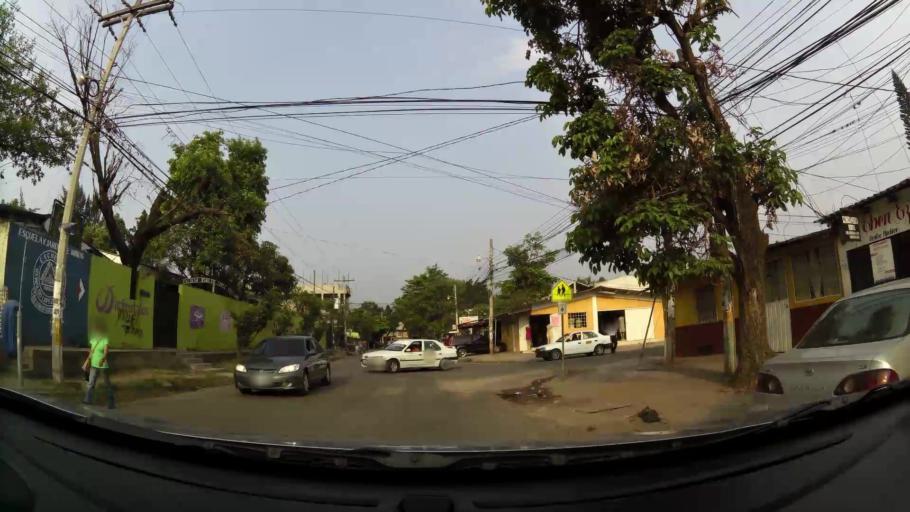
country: HN
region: Francisco Morazan
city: Tegucigalpa
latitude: 14.0683
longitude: -87.1783
